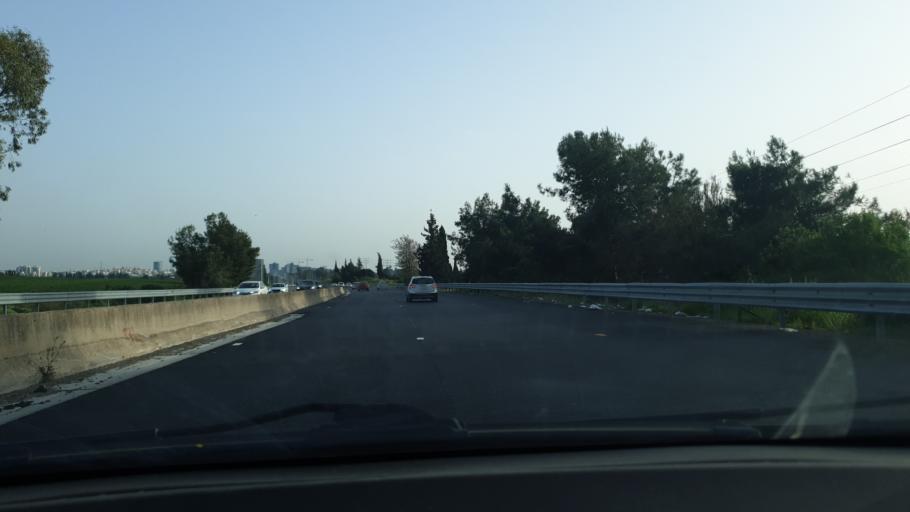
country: IL
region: Central District
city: Tel Mond
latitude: 32.2267
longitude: 34.8829
